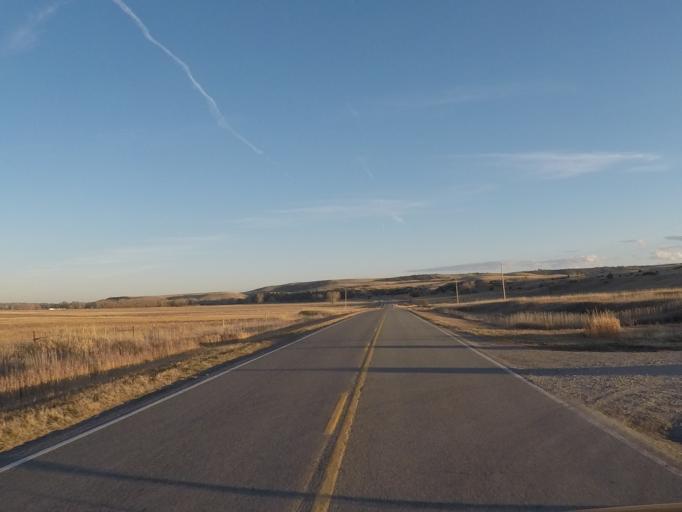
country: US
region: Montana
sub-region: Sweet Grass County
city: Big Timber
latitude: 45.7946
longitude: -109.8571
